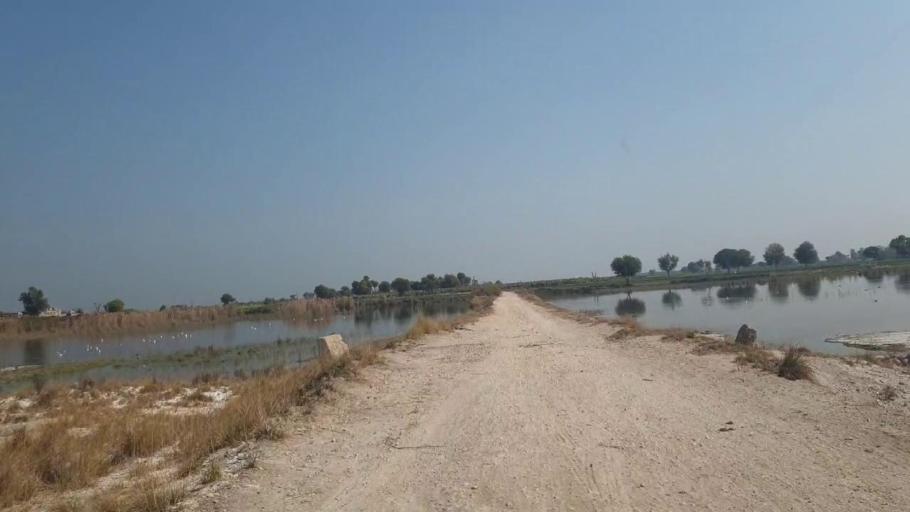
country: PK
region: Sindh
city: Sakrand
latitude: 26.0500
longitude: 68.4440
